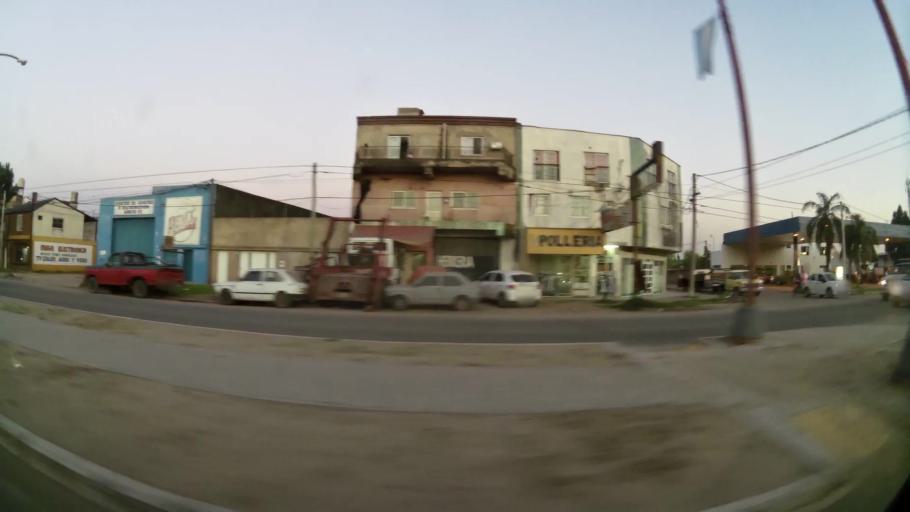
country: AR
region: Santa Fe
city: Santa Fe de la Vera Cruz
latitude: -31.6053
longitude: -60.7130
